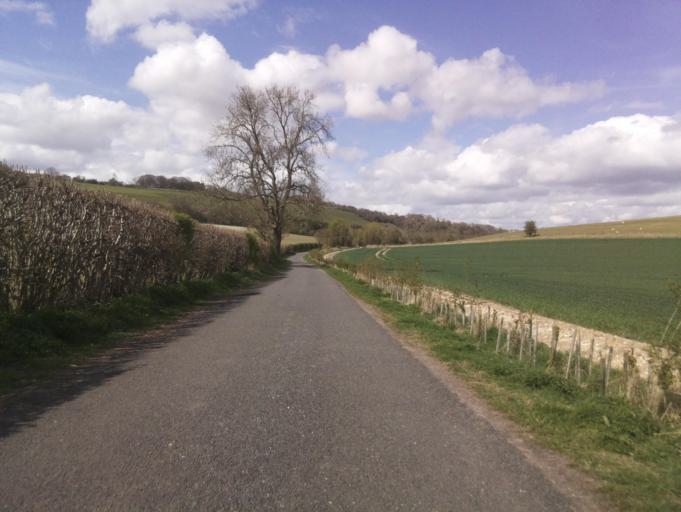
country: GB
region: England
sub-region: West Berkshire
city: Kintbury
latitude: 51.3324
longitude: -1.4688
